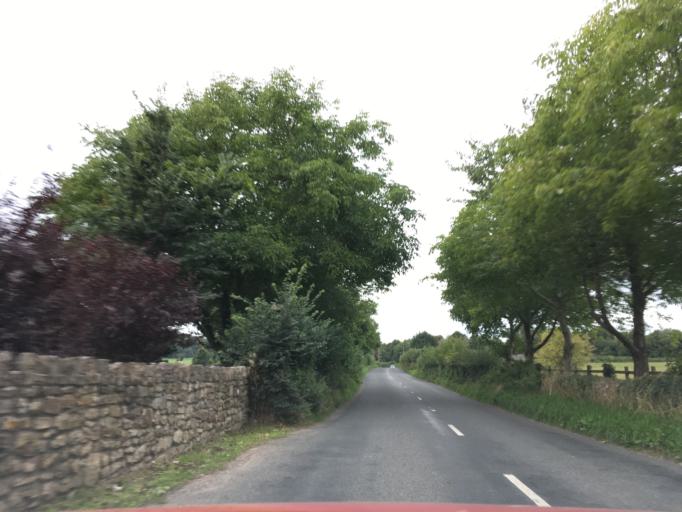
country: GB
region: Wales
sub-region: Monmouthshire
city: Rogiet
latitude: 51.6118
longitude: -2.7725
